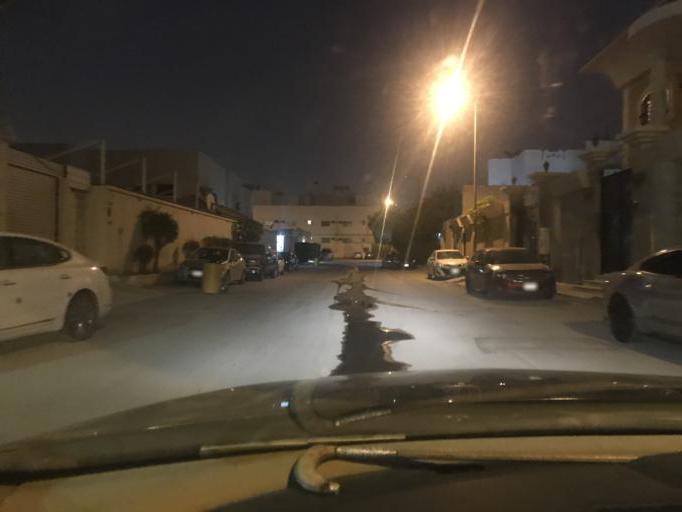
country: SA
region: Ar Riyad
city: Riyadh
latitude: 24.7498
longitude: 46.7751
